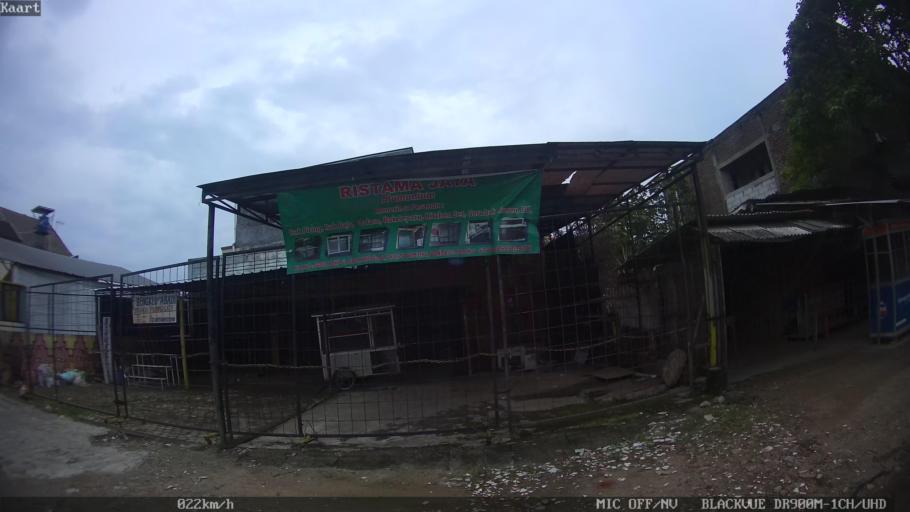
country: ID
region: Lampung
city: Kedaton
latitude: -5.3756
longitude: 105.2172
